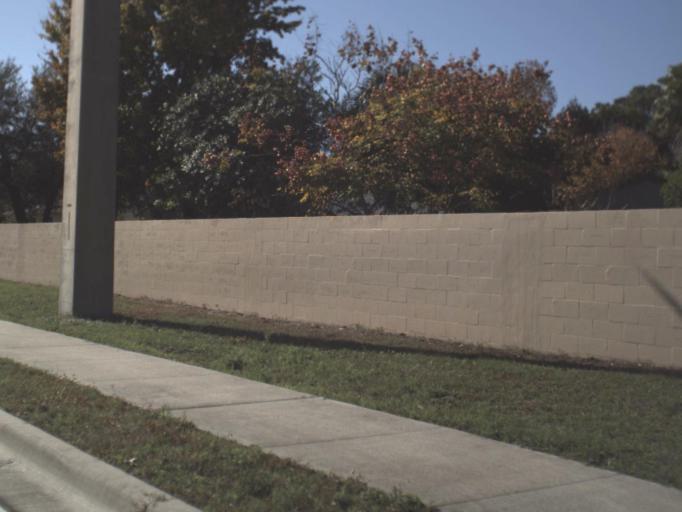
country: US
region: Florida
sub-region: Volusia County
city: Port Orange
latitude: 29.0945
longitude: -81.0289
